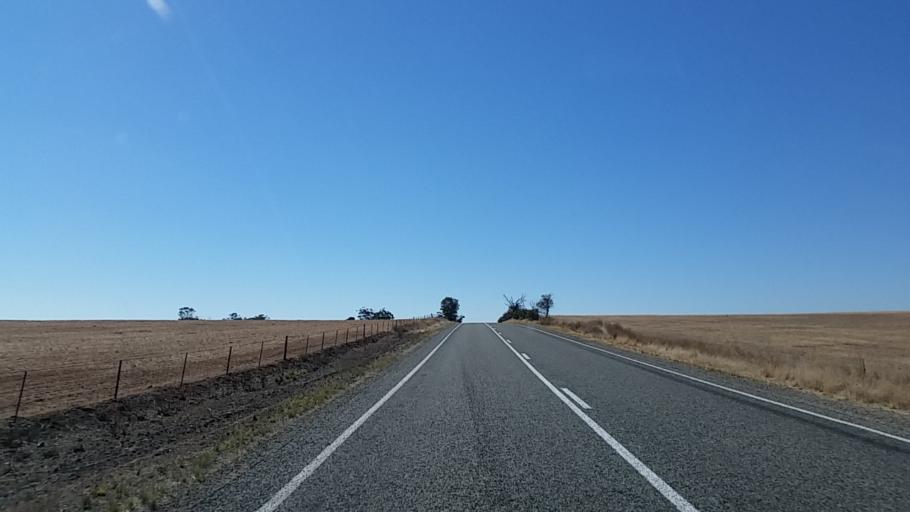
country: AU
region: South Australia
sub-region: Northern Areas
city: Jamestown
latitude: -33.3420
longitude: 138.8924
